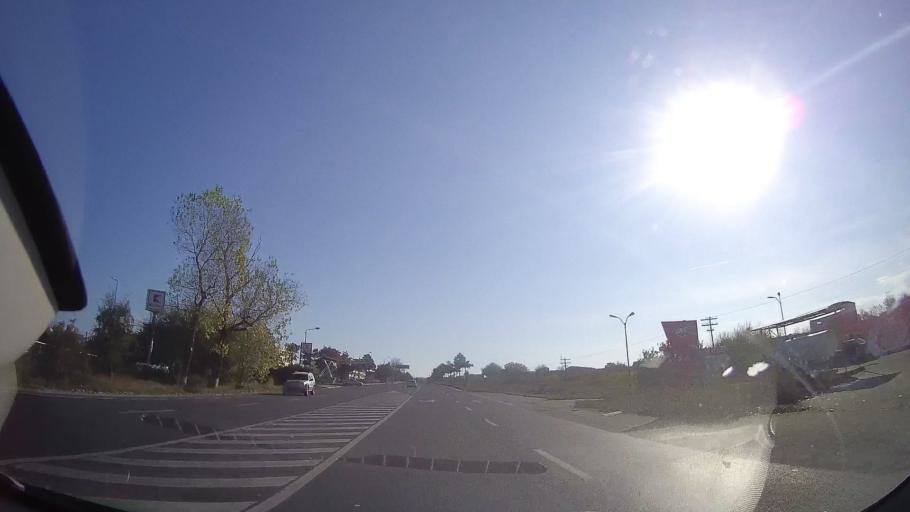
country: RO
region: Constanta
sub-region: Municipiul Mangalia
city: Mangalia
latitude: 43.8301
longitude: 28.5796
